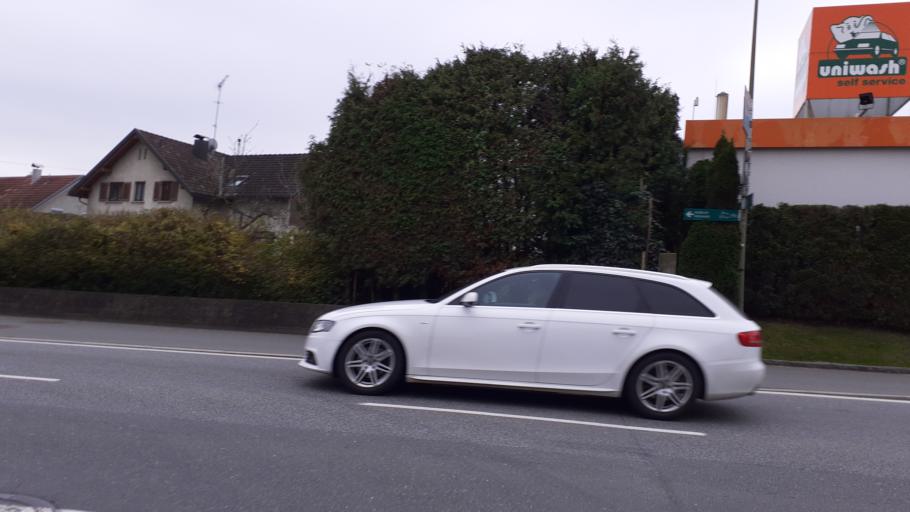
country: AT
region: Vorarlberg
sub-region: Politischer Bezirk Dornbirn
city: Lustenau
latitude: 47.4264
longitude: 9.6507
